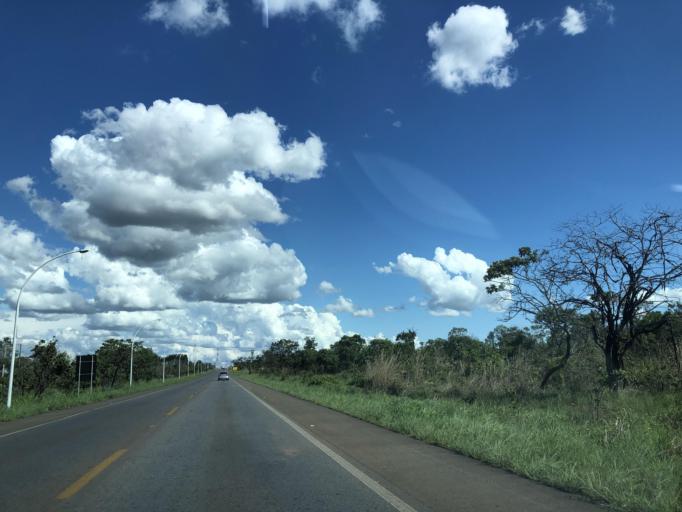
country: BR
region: Federal District
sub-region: Brasilia
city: Brasilia
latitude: -15.6787
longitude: -47.8716
